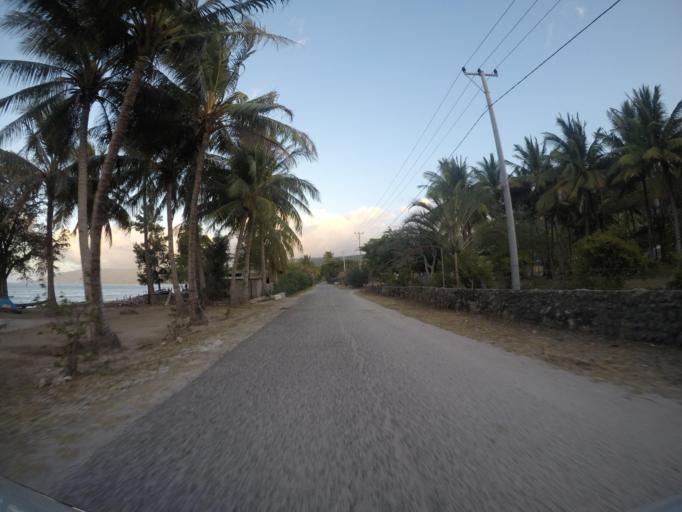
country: TL
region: Lautem
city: Lospalos
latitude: -8.3570
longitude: 127.0581
